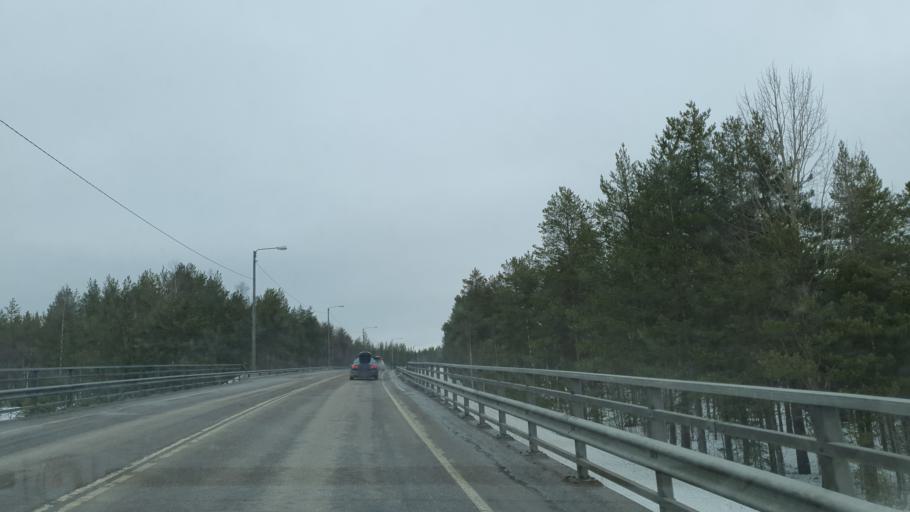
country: FI
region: Lapland
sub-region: Torniolaakso
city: Pello
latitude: 66.8310
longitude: 24.0014
